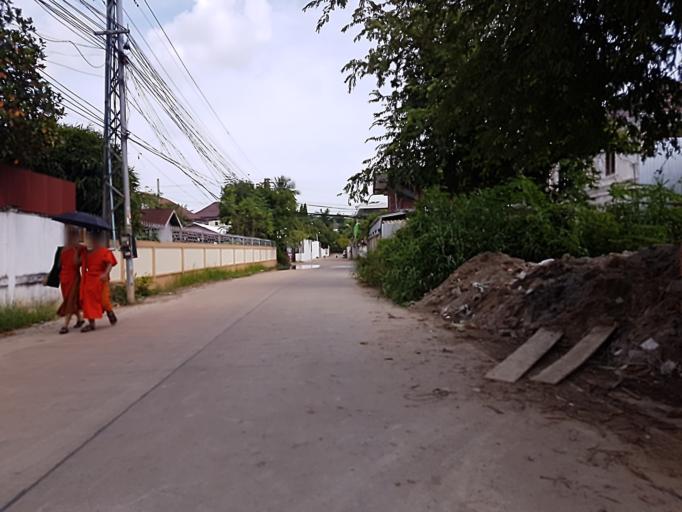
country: LA
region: Vientiane
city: Vientiane
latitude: 17.9476
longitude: 102.6233
